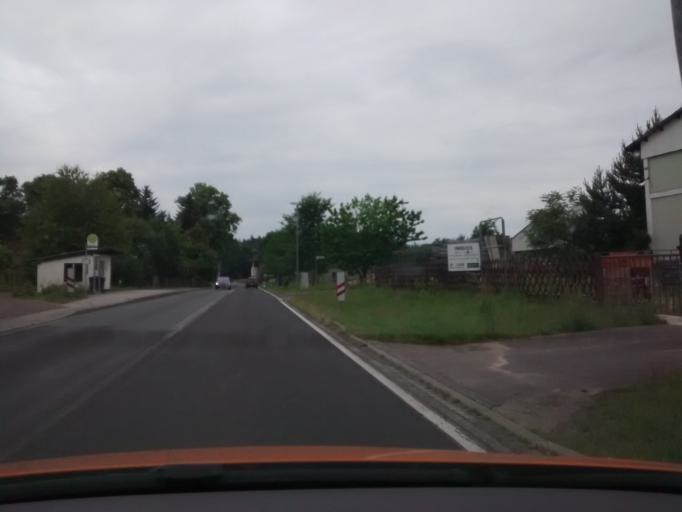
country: DE
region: Brandenburg
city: Wiesenburg
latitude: 52.1005
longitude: 12.4304
